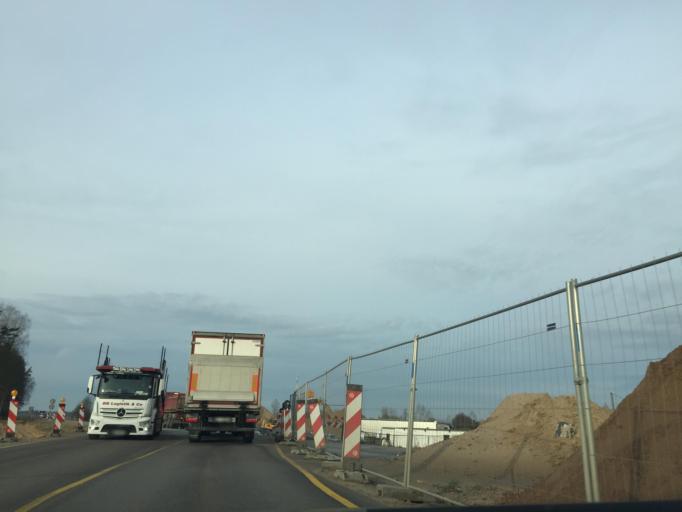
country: LV
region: Kekava
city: Kekava
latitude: 56.8086
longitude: 24.1946
